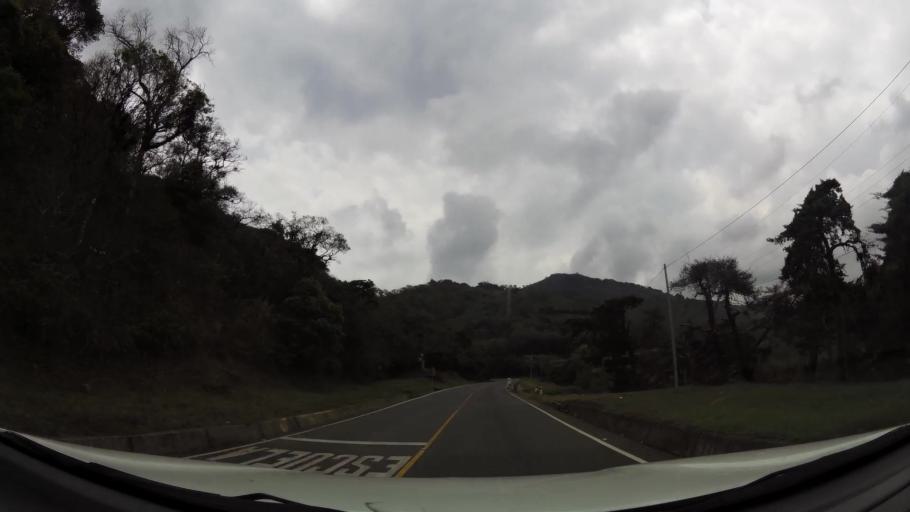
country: NI
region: Matagalpa
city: Matagalpa
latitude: 12.9756
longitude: -85.9211
